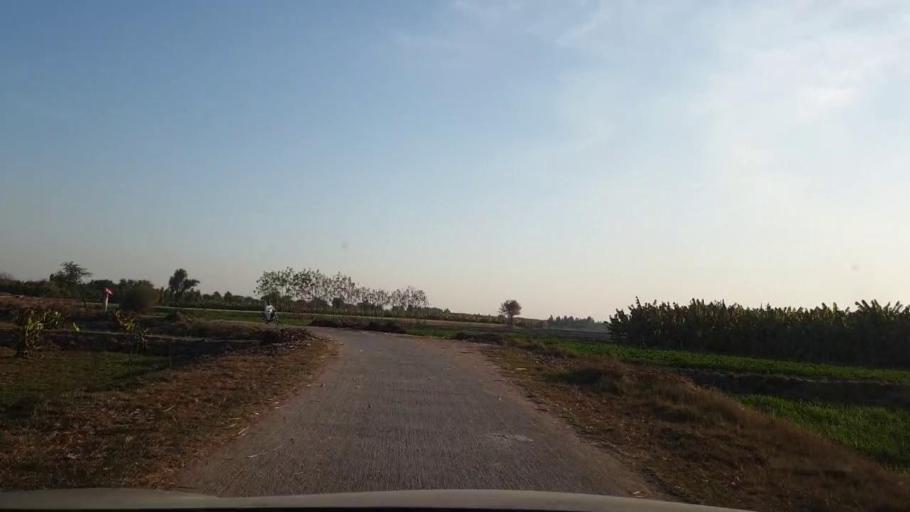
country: PK
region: Sindh
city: Tando Adam
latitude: 25.6200
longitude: 68.6702
